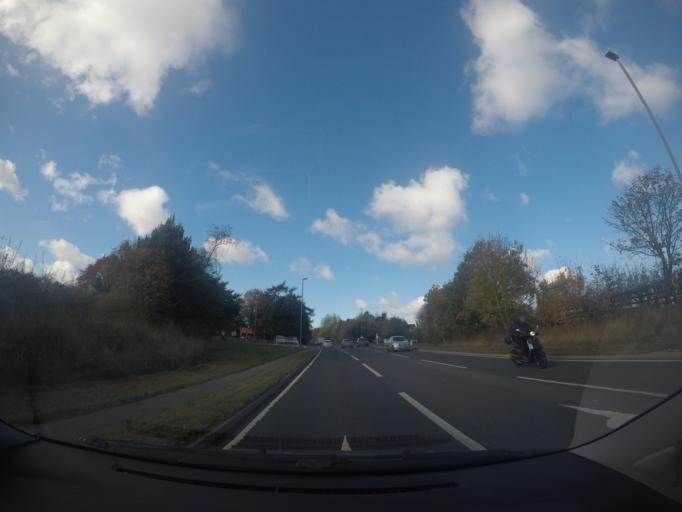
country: GB
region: England
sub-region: City and Borough of Leeds
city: Walton
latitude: 54.0024
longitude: -1.2956
